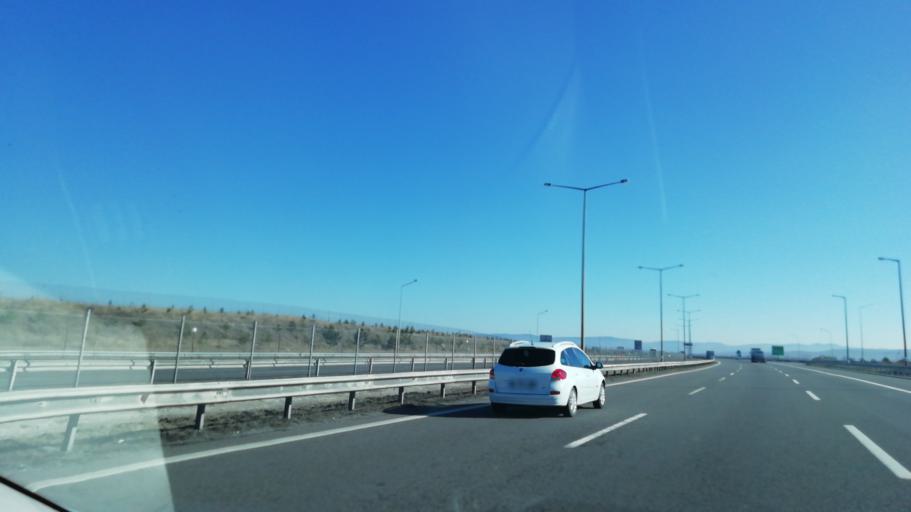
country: TR
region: Bolu
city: Dortdivan
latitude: 40.7489
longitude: 32.0856
